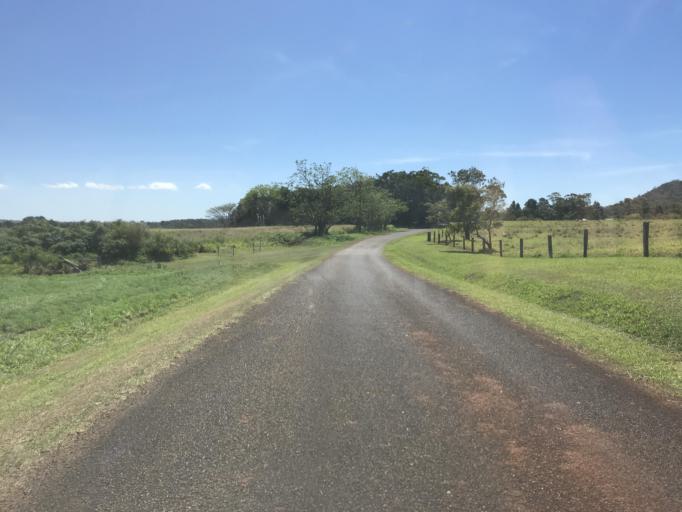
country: AU
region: Queensland
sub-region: Tablelands
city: Atherton
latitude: -17.2760
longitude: 145.5445
